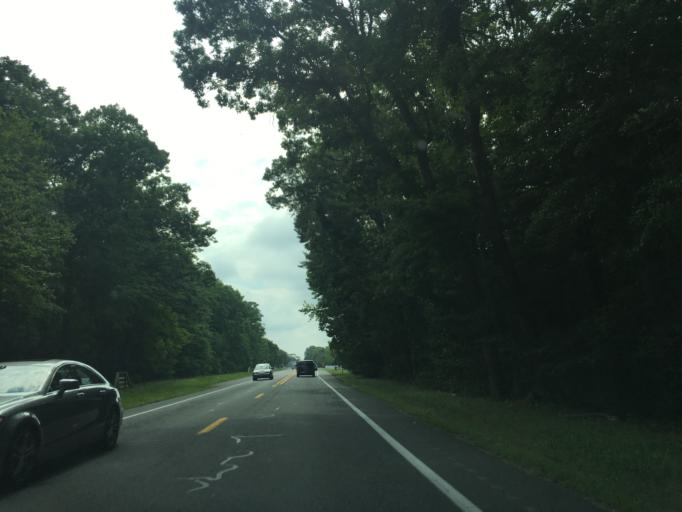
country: US
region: Delaware
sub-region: Sussex County
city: Ocean View
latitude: 38.5558
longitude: -75.0778
